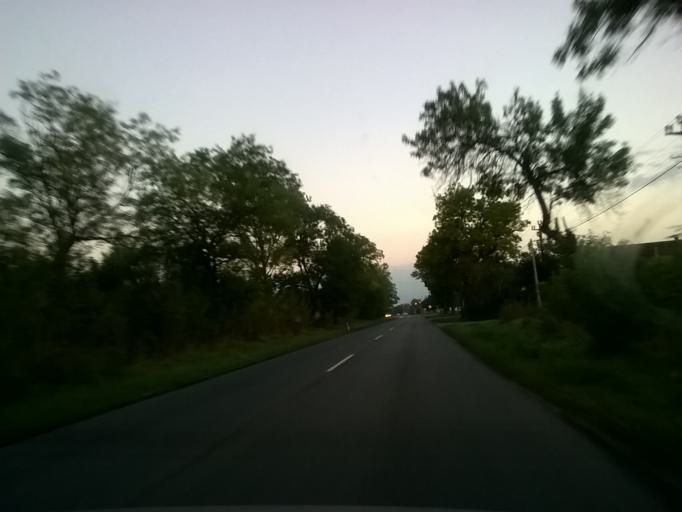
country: RS
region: Autonomna Pokrajina Vojvodina
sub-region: Juznobanatski Okrug
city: Pancevo
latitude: 44.9046
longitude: 20.6316
